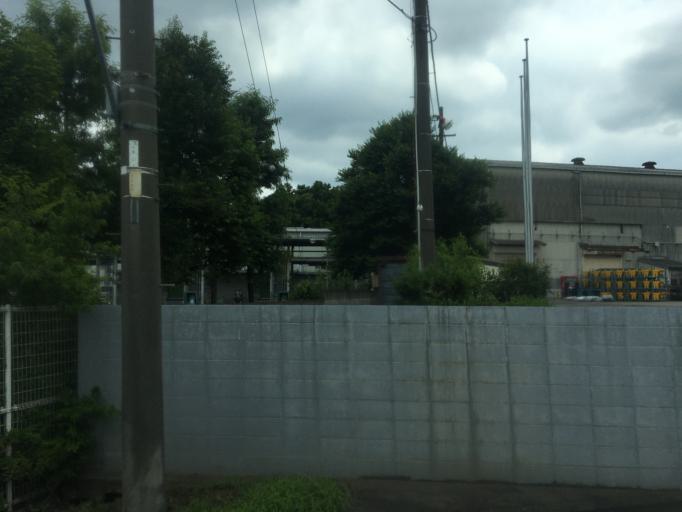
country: JP
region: Saitama
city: Ageoshimo
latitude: 35.9414
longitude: 139.5663
